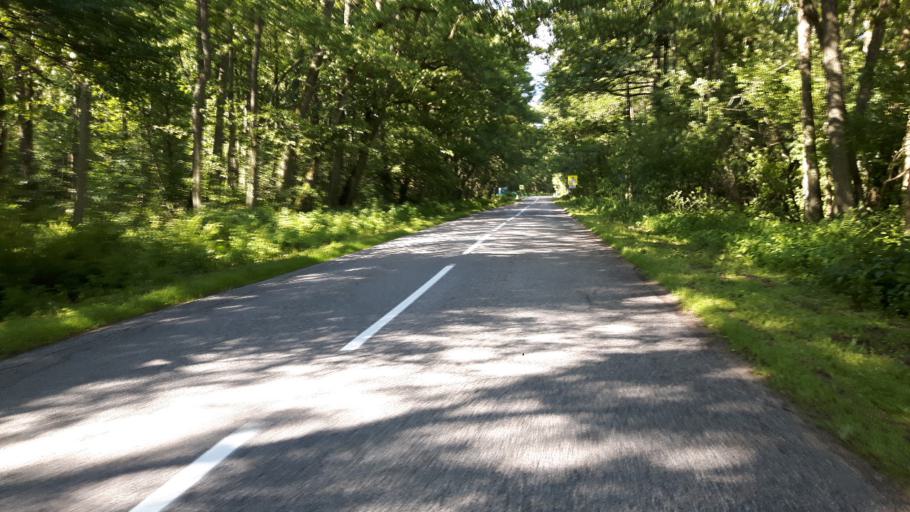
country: LT
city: Nida
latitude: 55.1494
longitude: 20.8187
